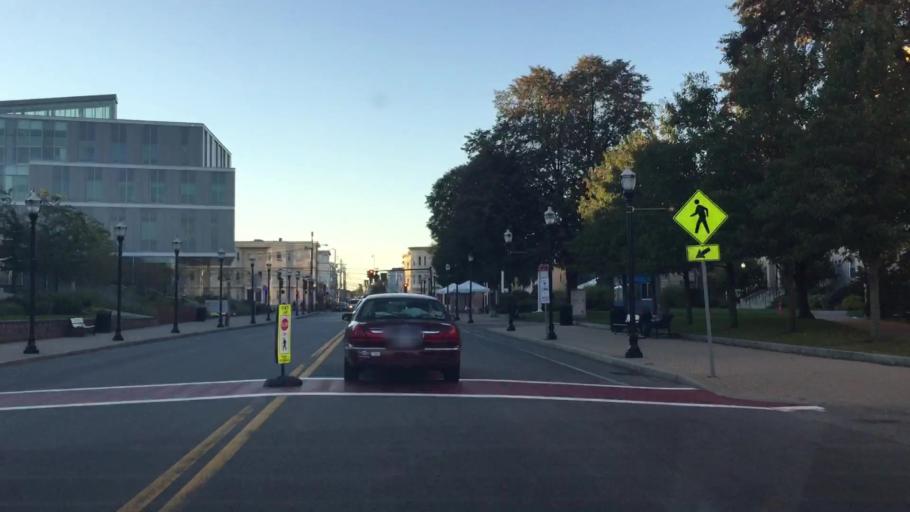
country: US
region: Massachusetts
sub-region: Middlesex County
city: Lowell
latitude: 42.6528
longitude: -71.3256
